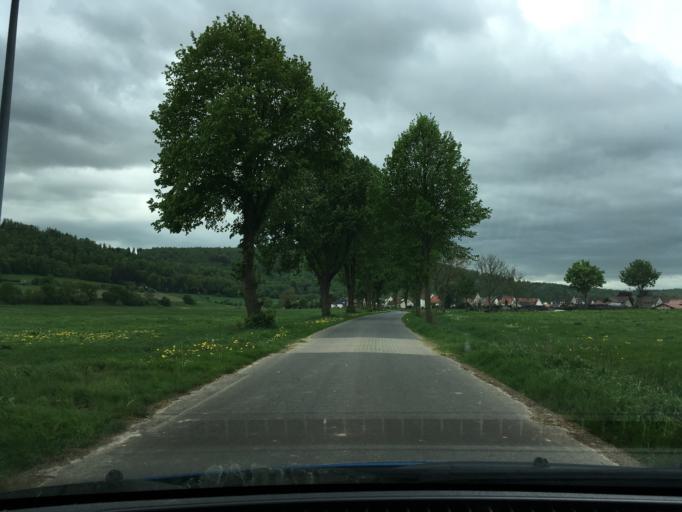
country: DE
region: Lower Saxony
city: Bodenfelde
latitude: 51.6339
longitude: 9.5328
